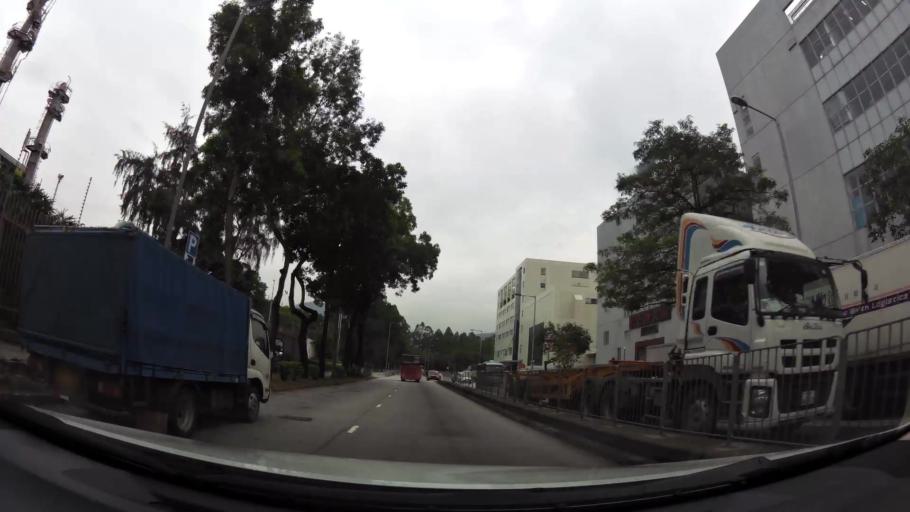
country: HK
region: Tai Po
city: Tai Po
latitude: 22.4545
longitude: 114.1812
